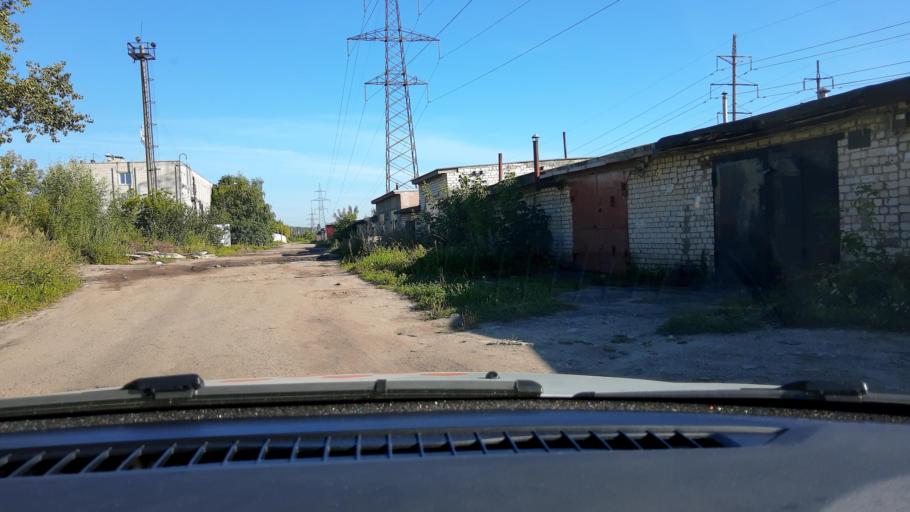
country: RU
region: Nizjnij Novgorod
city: Nizhniy Novgorod
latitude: 56.2740
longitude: 43.8967
